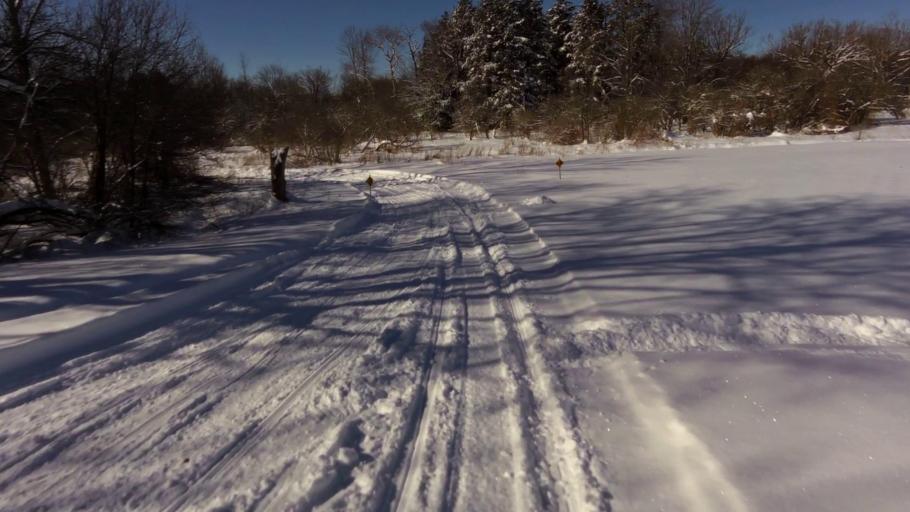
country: US
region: New York
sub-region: Chautauqua County
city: Silver Creek
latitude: 42.3740
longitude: -79.1522
